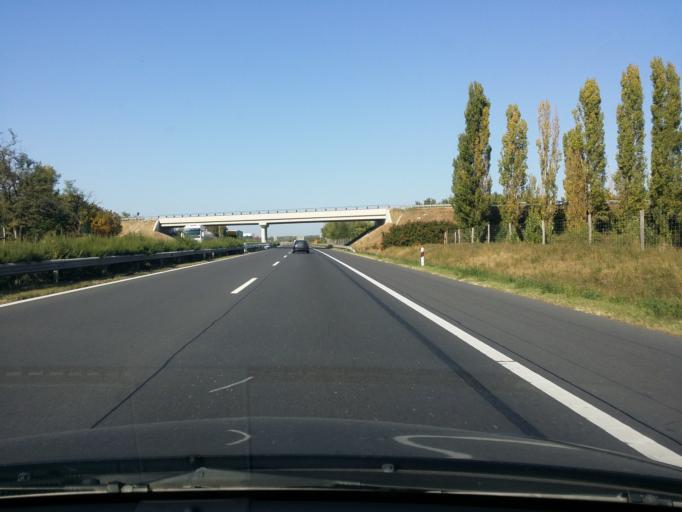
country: HU
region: Bacs-Kiskun
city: Kecskemet
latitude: 46.9503
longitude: 19.6204
